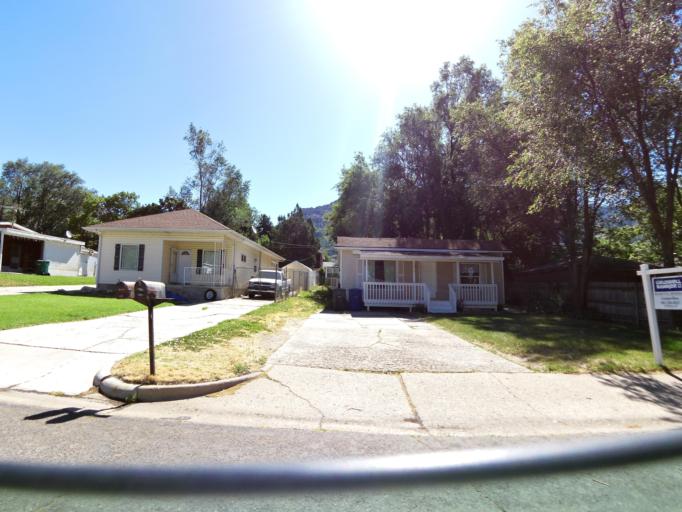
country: US
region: Utah
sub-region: Weber County
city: Ogden
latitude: 41.2291
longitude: -111.9423
